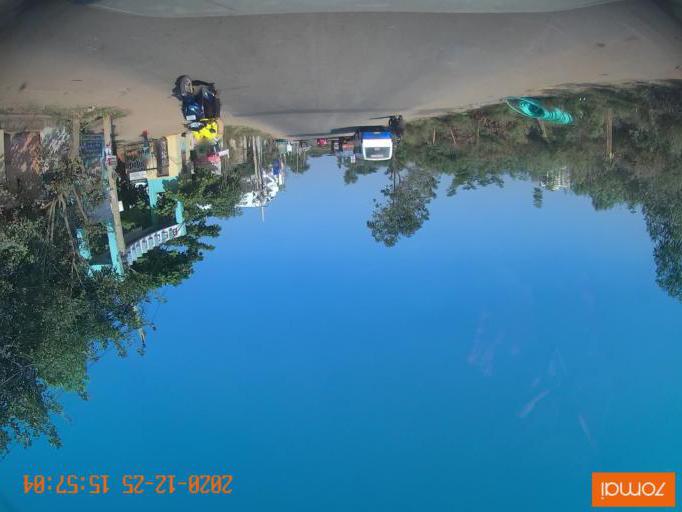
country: IN
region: Karnataka
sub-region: Bangalore Urban
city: Bangalore
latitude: 12.8681
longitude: 77.6211
